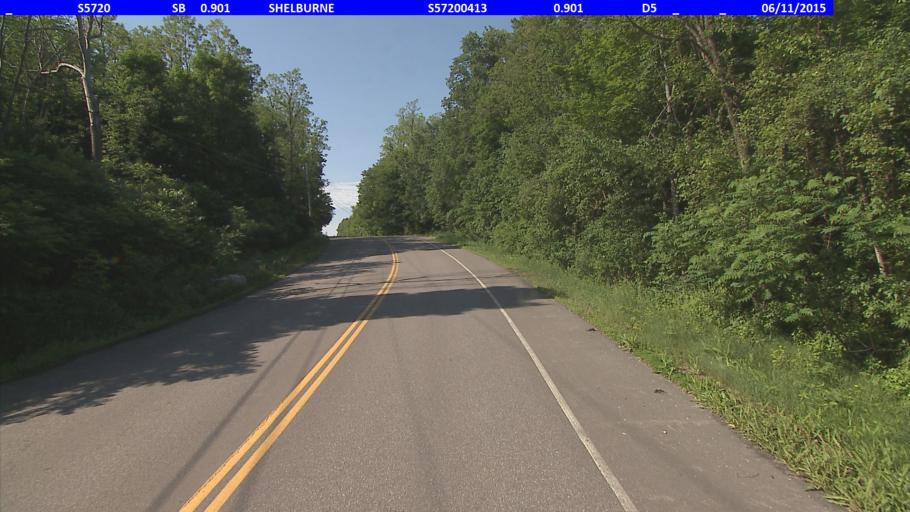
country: US
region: Vermont
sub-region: Chittenden County
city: South Burlington
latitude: 44.3810
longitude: -73.2020
